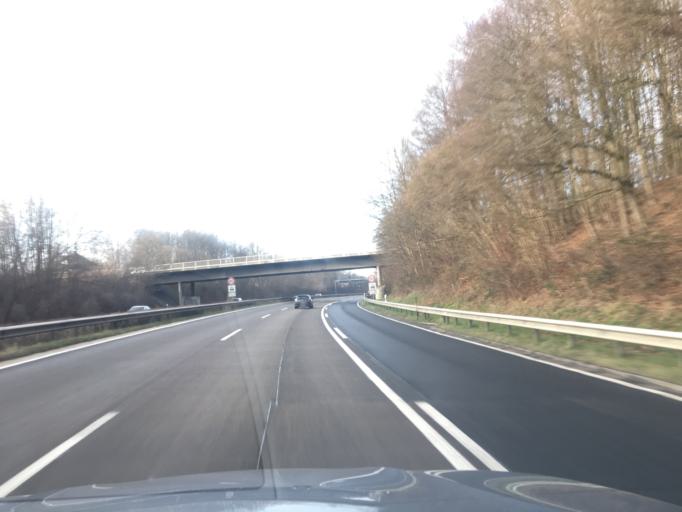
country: DE
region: Rheinland-Pfalz
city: Hohr-Grenzhausen
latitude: 50.4441
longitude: 7.6650
